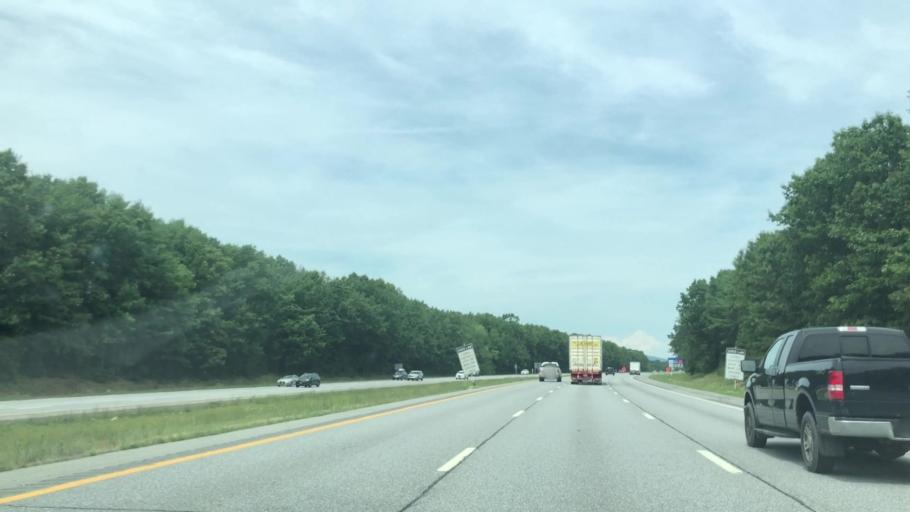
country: US
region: New York
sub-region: Warren County
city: West Glens Falls
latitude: 43.2883
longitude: -73.6810
